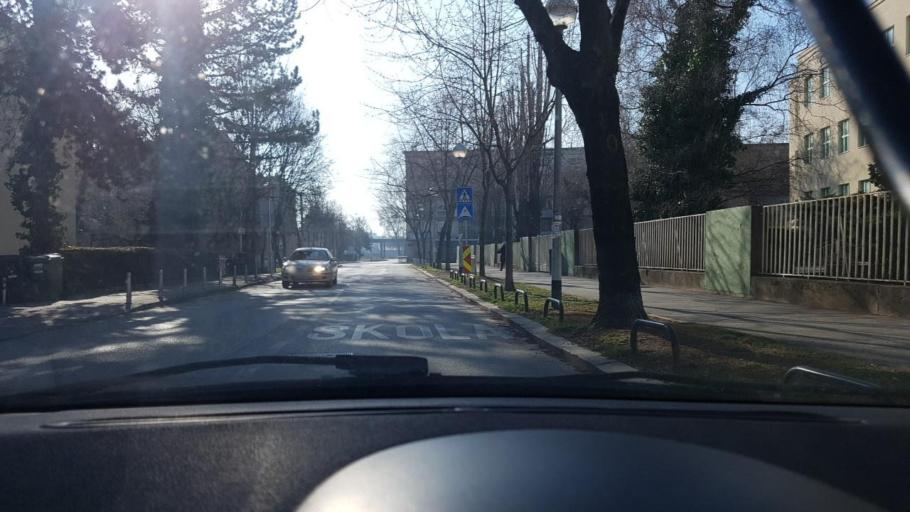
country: HR
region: Grad Zagreb
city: Zagreb
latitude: 45.8122
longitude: 16.0081
